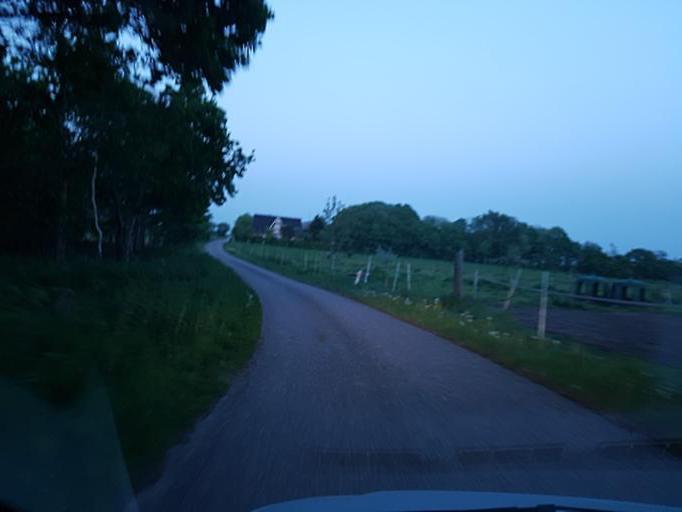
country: DK
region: South Denmark
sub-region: Esbjerg Kommune
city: Tjaereborg
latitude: 55.5106
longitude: 8.5630
